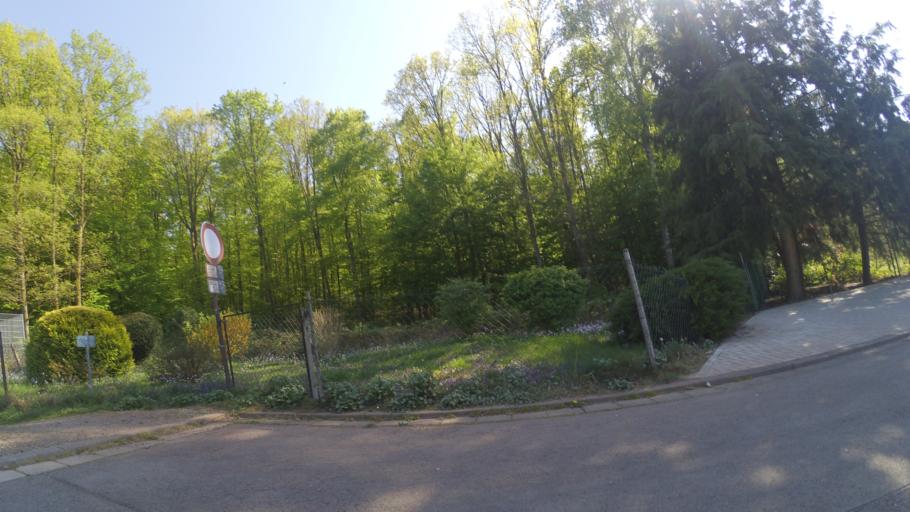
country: DE
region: Saarland
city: Hangard
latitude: 49.3657
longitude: 7.2009
